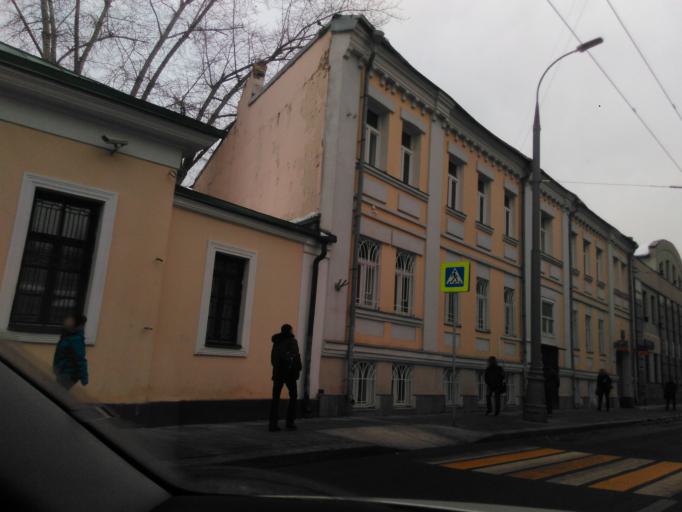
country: RU
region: Moscow
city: Zamoskvorech'ye
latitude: 55.7316
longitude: 37.6208
